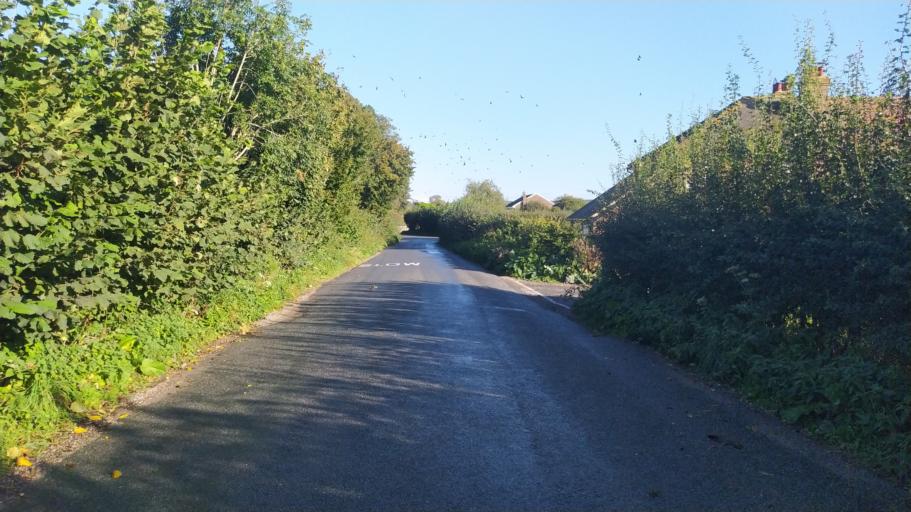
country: GB
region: England
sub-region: Dorset
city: Blandford Forum
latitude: 50.7747
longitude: -2.1669
